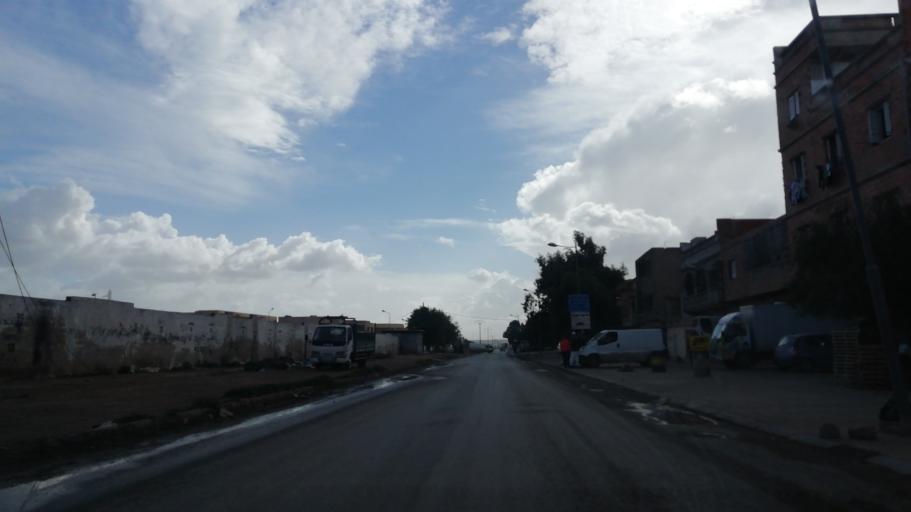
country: DZ
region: Oran
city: Sidi ech Chahmi
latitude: 35.6498
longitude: -0.5642
